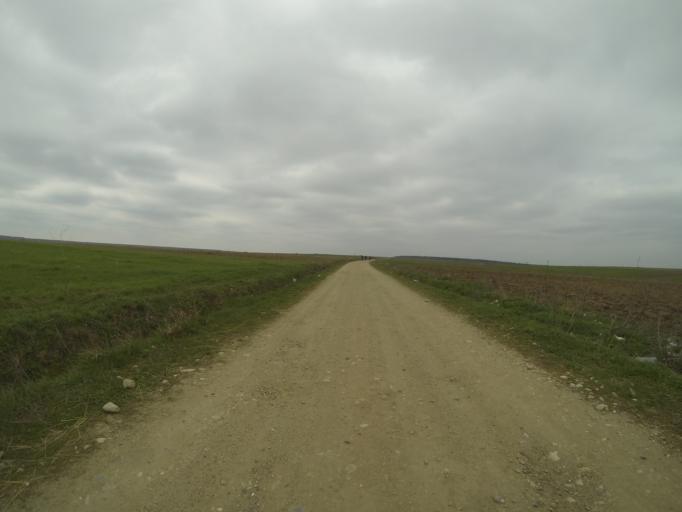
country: RO
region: Dolj
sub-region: Comuna Breasta
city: Breasta
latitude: 44.3401
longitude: 23.6601
